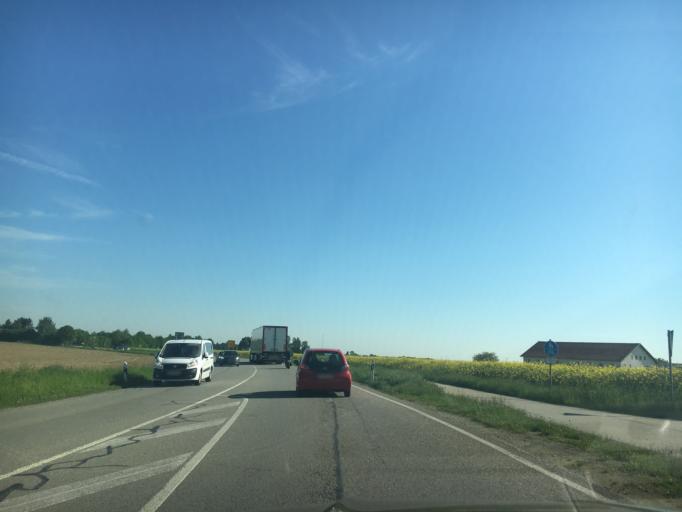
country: DE
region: Bavaria
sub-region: Upper Bavaria
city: Unterneukirchen
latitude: 48.1752
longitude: 12.6306
